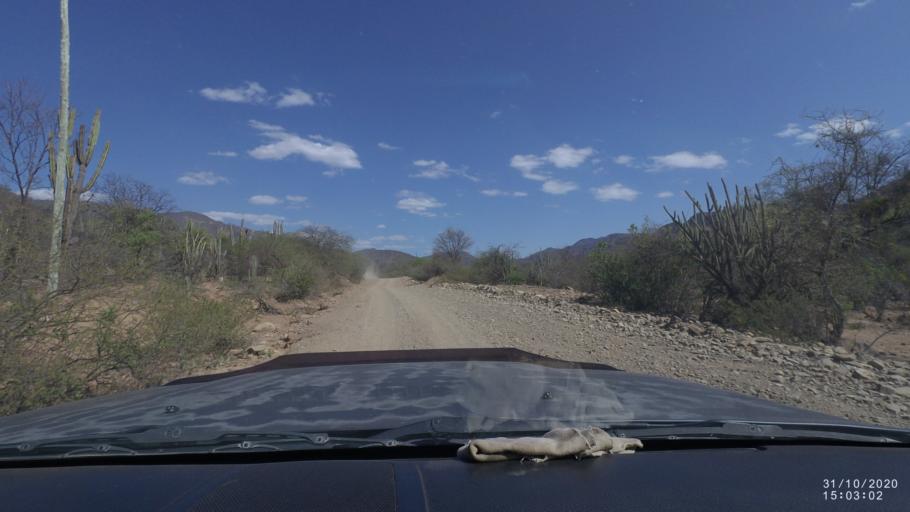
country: BO
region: Cochabamba
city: Aiquile
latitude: -18.2733
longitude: -64.8091
